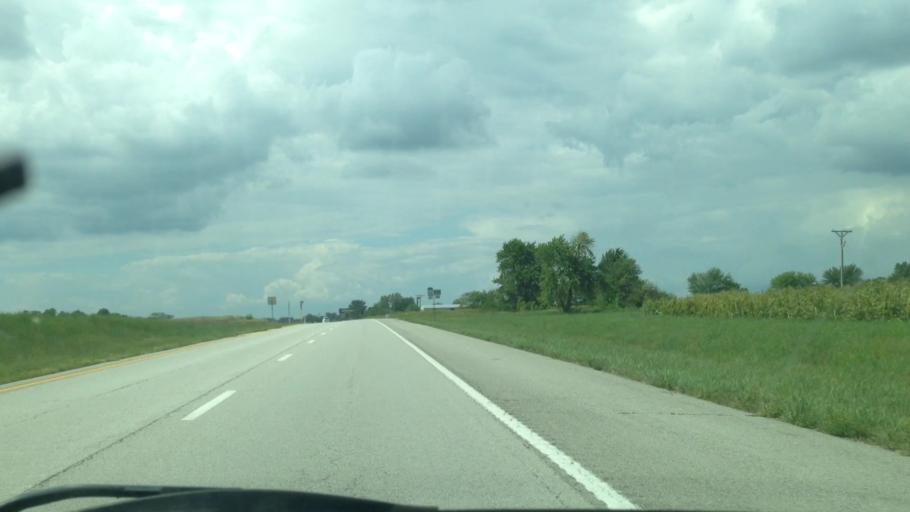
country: US
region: Missouri
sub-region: Pike County
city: Bowling Green
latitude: 39.2698
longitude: -91.0826
